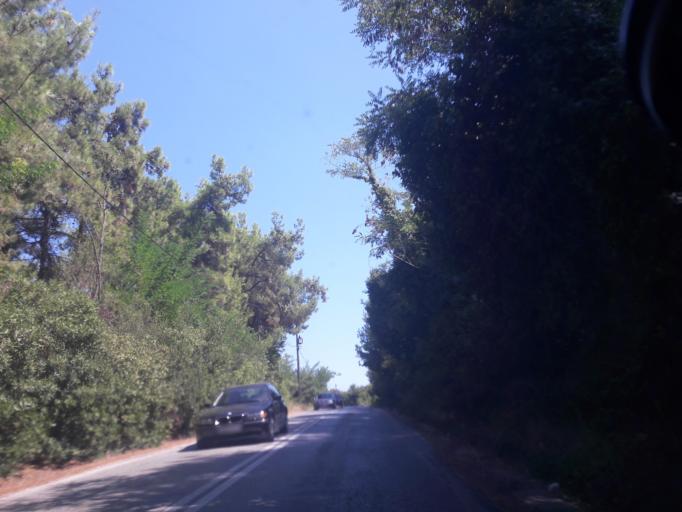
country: GR
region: Central Macedonia
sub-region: Nomos Chalkidikis
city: Nea Roda
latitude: 40.3850
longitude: 23.8980
